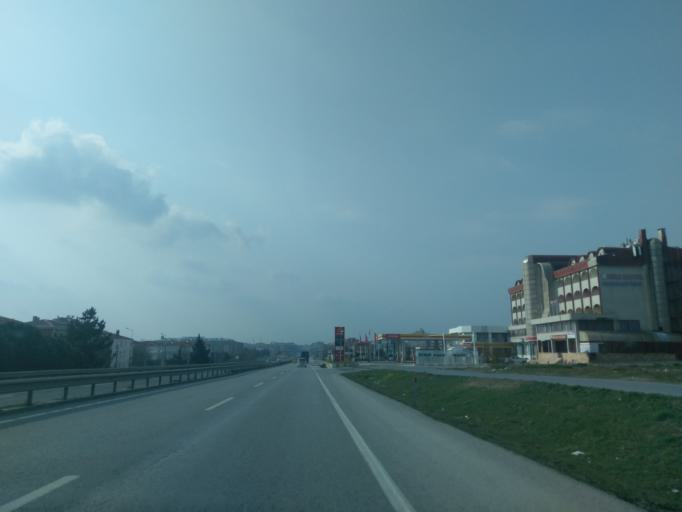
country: TR
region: Istanbul
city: Selimpasa
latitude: 41.0511
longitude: 28.3882
